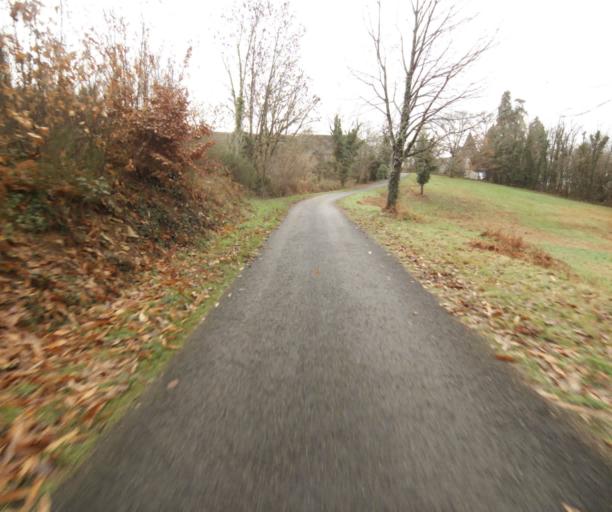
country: FR
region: Limousin
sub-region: Departement de la Correze
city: Saint-Mexant
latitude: 45.2754
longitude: 1.6410
